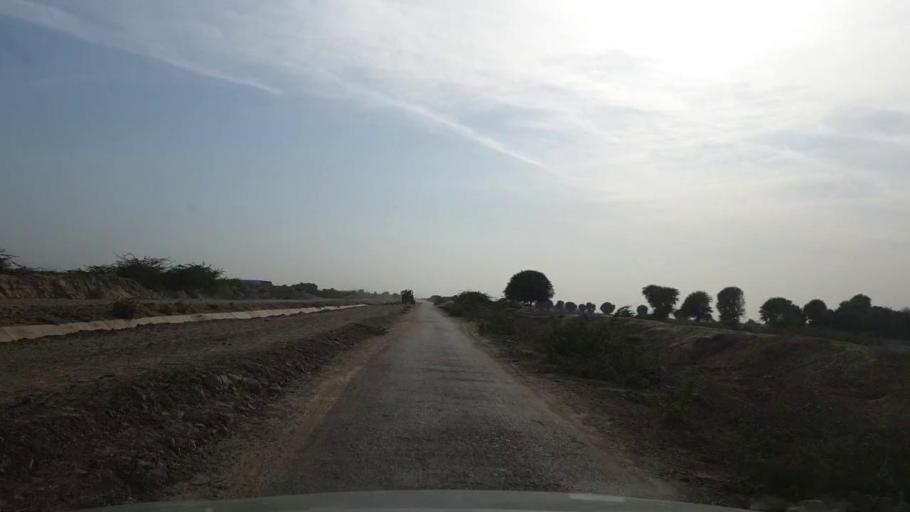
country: PK
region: Sindh
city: Kunri
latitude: 25.1580
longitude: 69.5143
